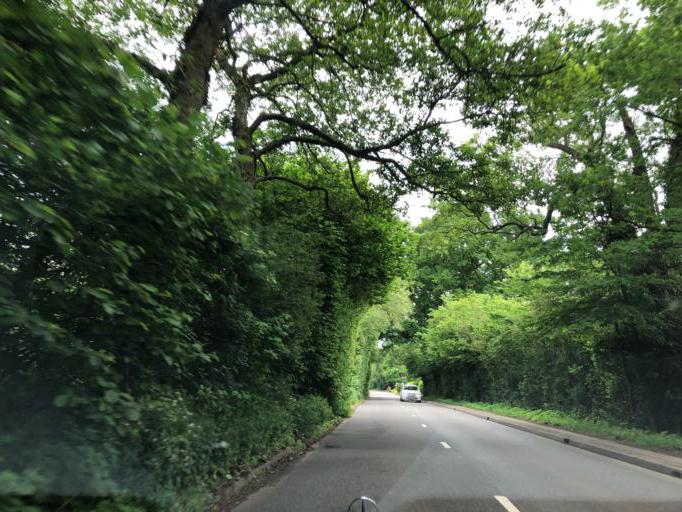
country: GB
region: England
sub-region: Solihull
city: Berkswell
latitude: 52.3960
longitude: -1.6010
